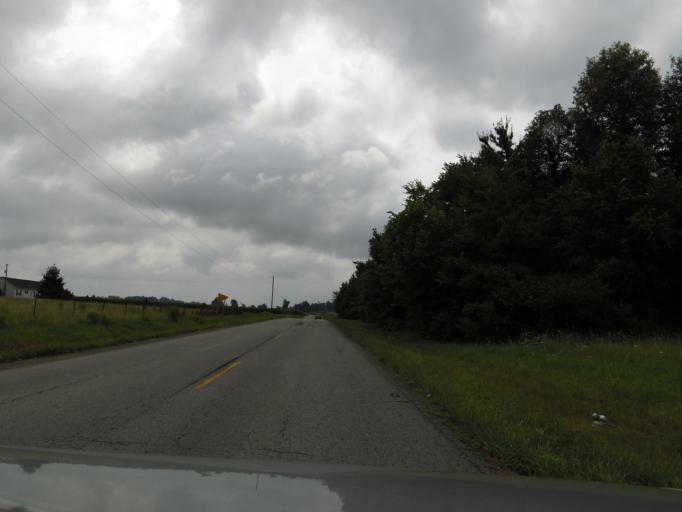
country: US
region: Kentucky
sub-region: Hopkins County
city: Madisonville
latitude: 37.3324
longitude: -87.4133
